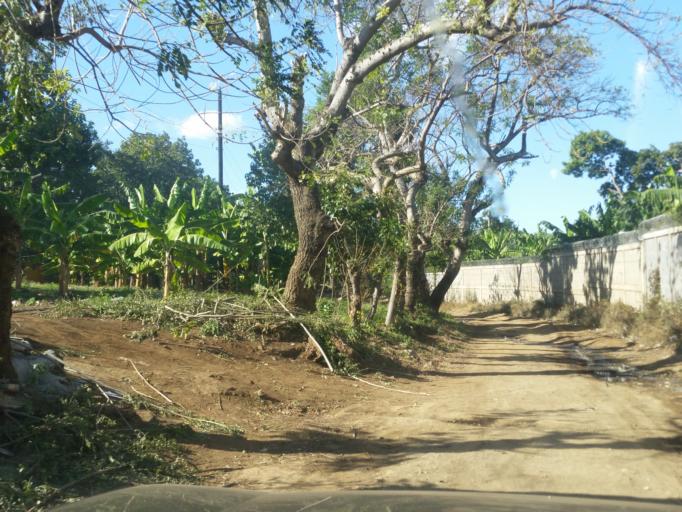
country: NI
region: Masaya
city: Ticuantepe
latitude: 12.0637
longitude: -86.2529
